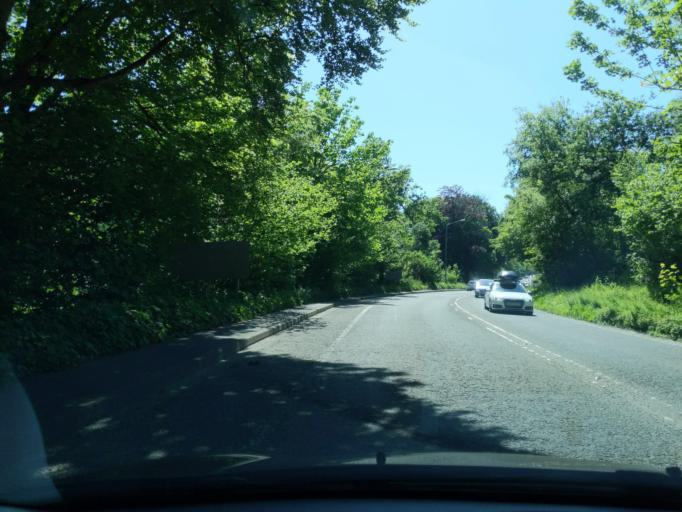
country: GB
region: England
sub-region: Cornwall
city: St Austell
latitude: 50.3443
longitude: -4.7457
